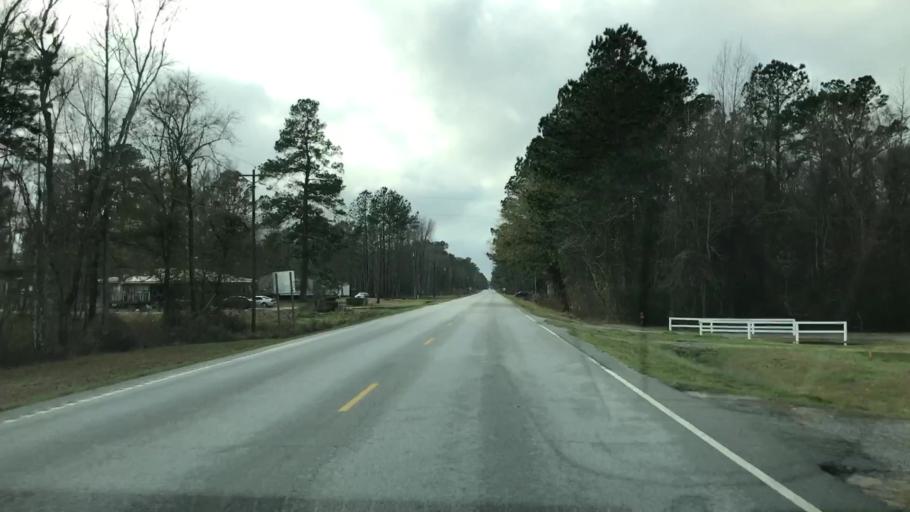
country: US
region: South Carolina
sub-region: Williamsburg County
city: Andrews
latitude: 33.2864
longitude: -79.7027
